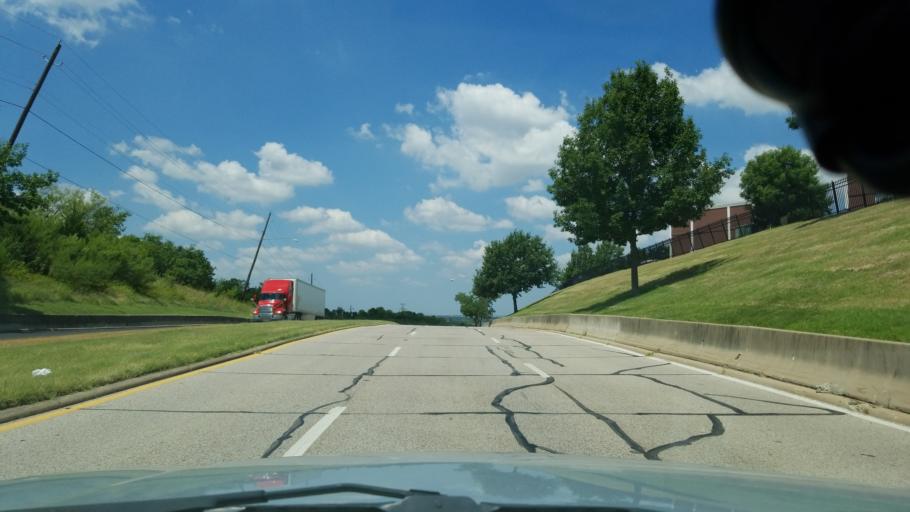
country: US
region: Texas
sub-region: Dallas County
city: Duncanville
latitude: 32.7058
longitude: -96.9453
